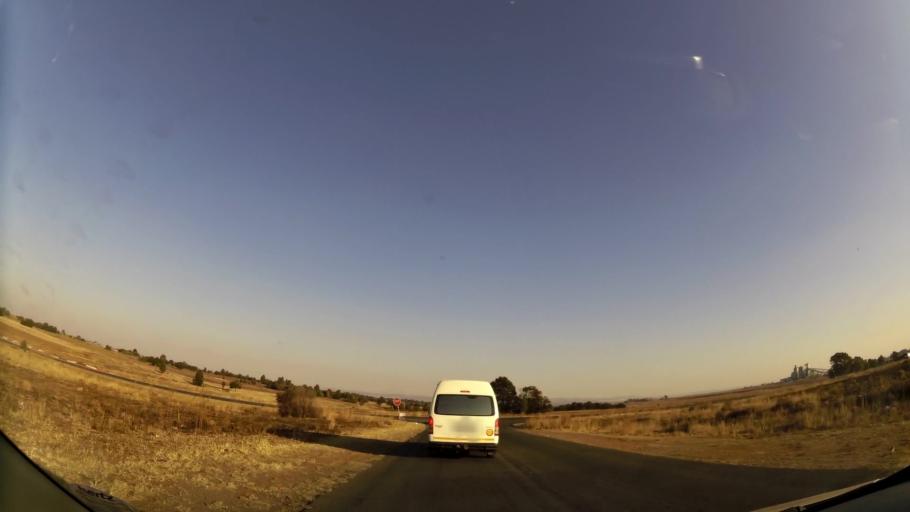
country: ZA
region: Gauteng
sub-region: West Rand District Municipality
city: Randfontein
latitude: -26.2015
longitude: 27.6747
